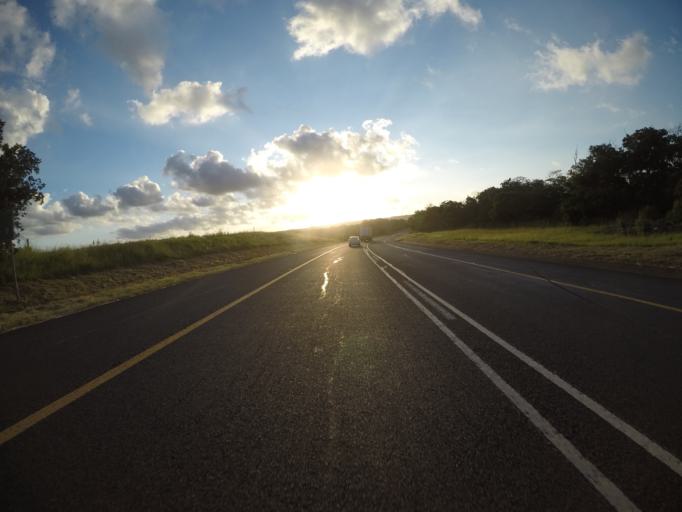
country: ZA
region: KwaZulu-Natal
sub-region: uThungulu District Municipality
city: Richards Bay
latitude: -28.6965
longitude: 32.0165
